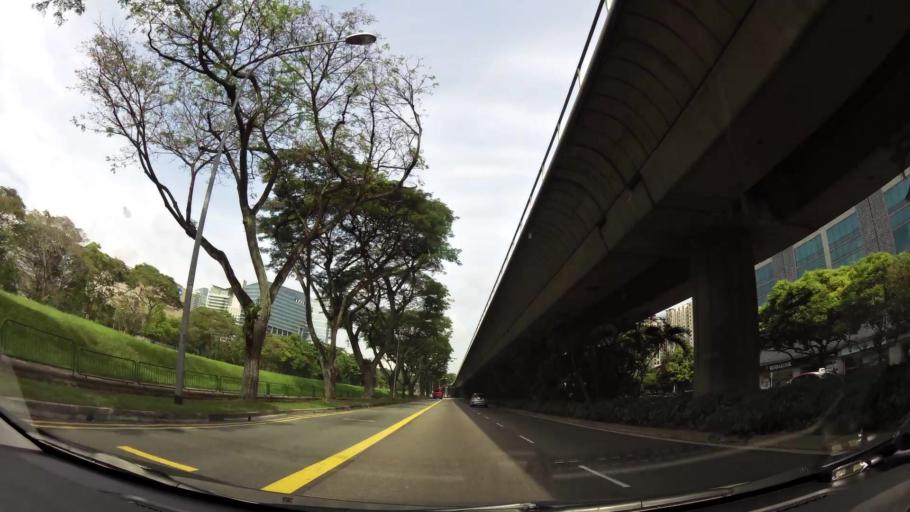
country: SG
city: Singapore
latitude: 1.3042
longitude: 103.7961
